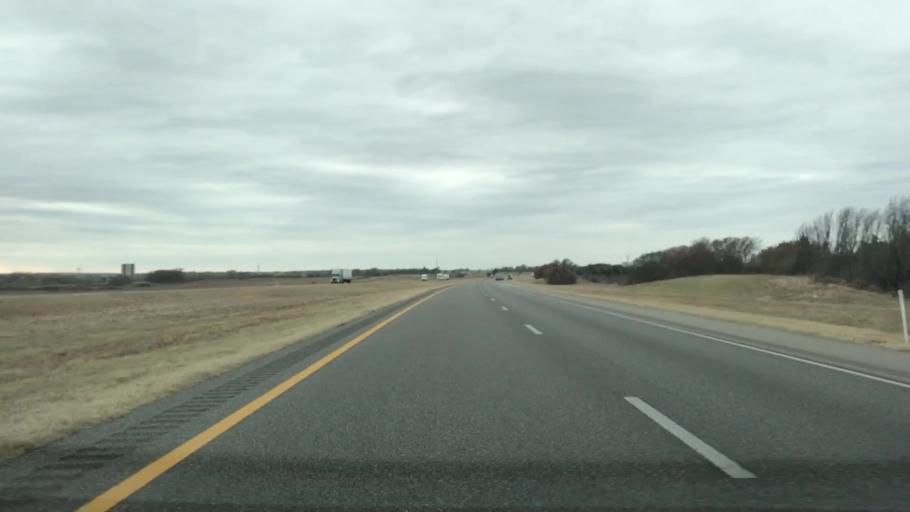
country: US
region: Oklahoma
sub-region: Beckham County
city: Erick
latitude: 35.2267
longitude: -99.9138
